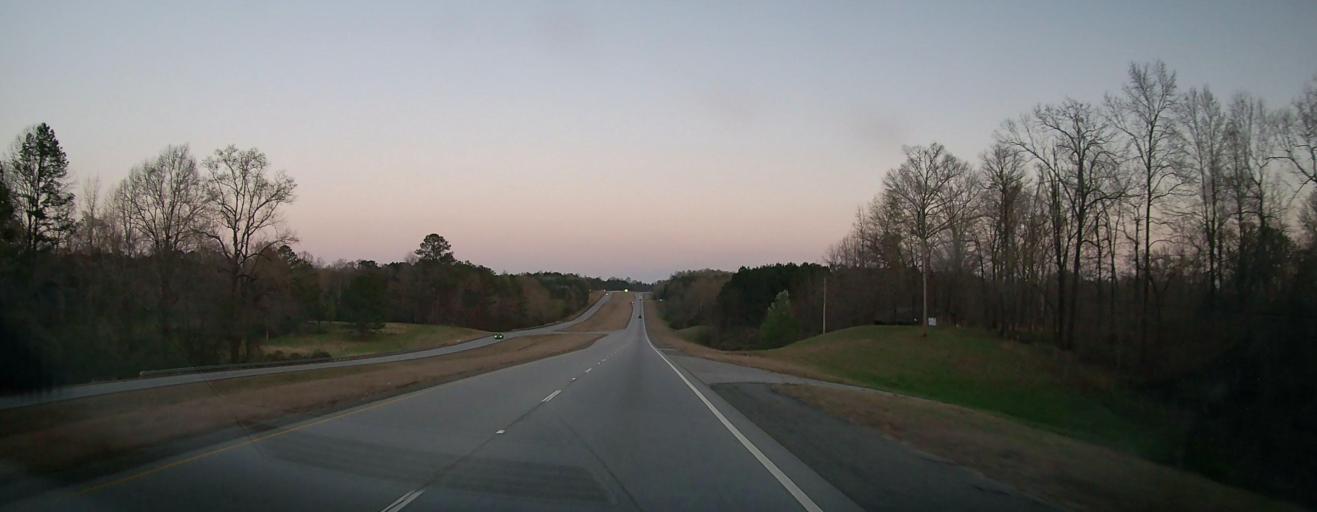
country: US
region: Alabama
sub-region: Tallapoosa County
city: Dadeville
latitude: 32.8752
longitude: -85.8127
